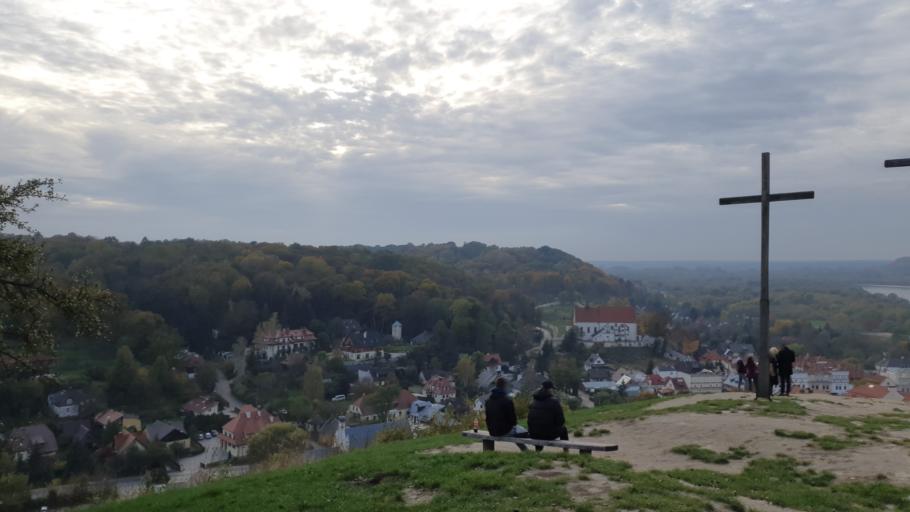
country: PL
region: Lublin Voivodeship
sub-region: Powiat pulawski
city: Kazimierz Dolny
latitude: 51.3219
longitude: 21.9509
